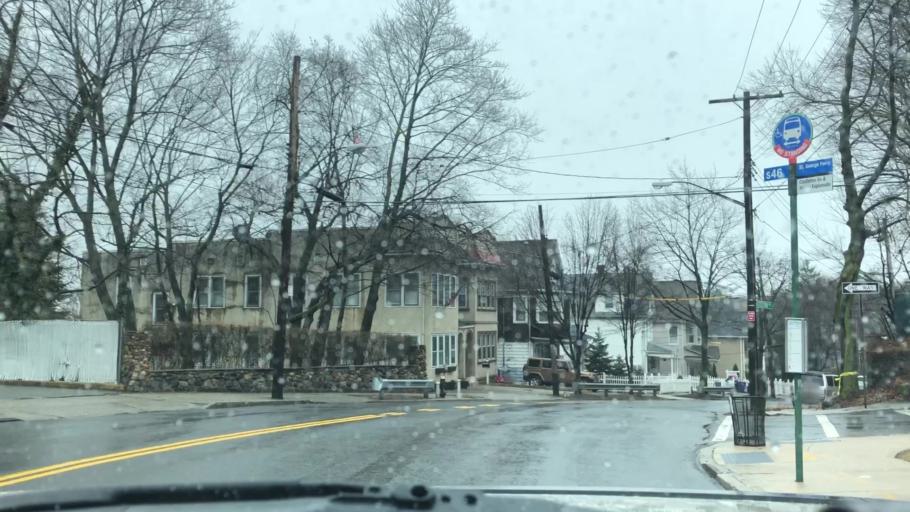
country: US
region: New Jersey
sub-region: Hudson County
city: Bayonne
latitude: 40.6333
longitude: -74.0922
